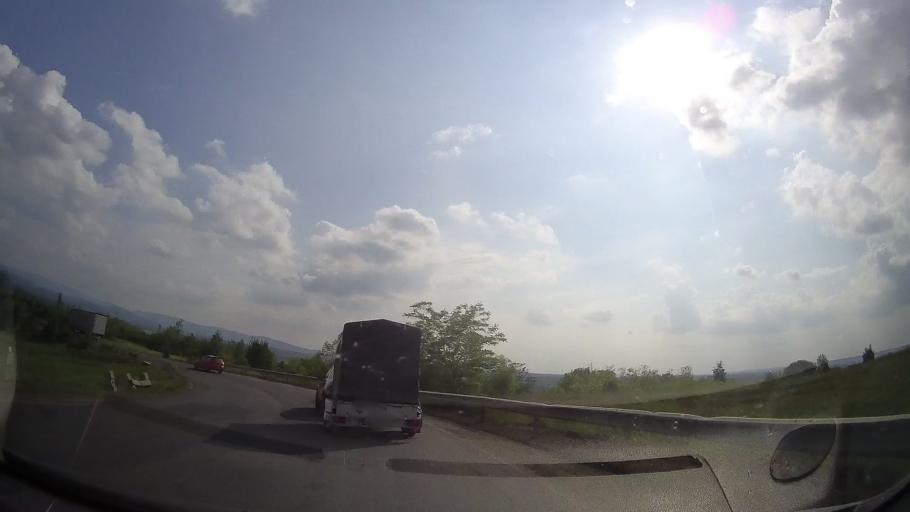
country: RO
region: Timis
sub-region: Comuna Curtea
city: Curtea
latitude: 45.8504
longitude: 22.3225
